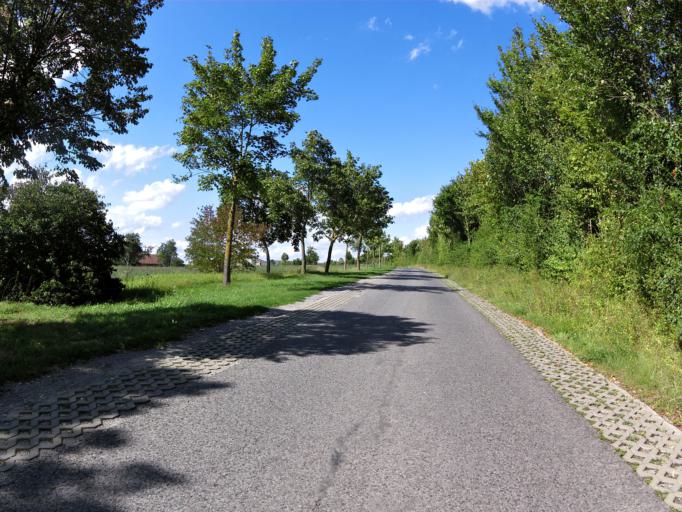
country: DE
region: Bavaria
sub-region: Regierungsbezirk Unterfranken
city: Marktsteft
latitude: 49.6920
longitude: 10.1437
